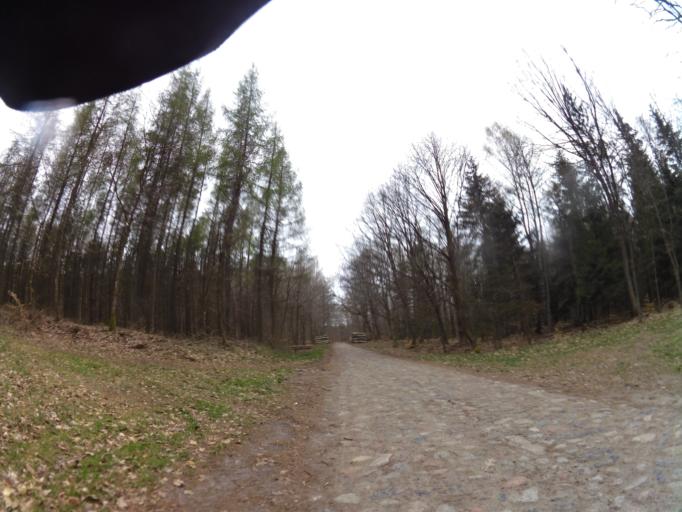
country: PL
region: West Pomeranian Voivodeship
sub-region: Powiat koszalinski
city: Bobolice
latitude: 53.9805
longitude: 16.6428
